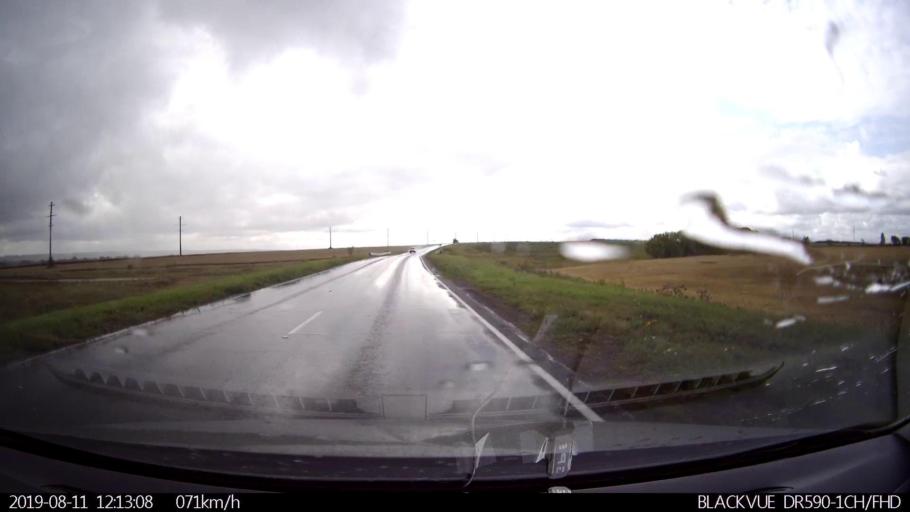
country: RU
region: Ulyanovsk
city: Silikatnyy
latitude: 53.9650
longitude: 47.9938
